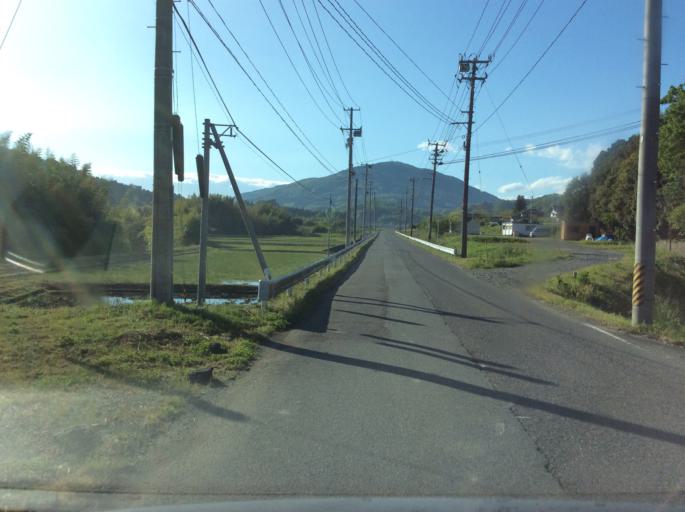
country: JP
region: Fukushima
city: Iwaki
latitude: 36.9883
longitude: 140.8307
